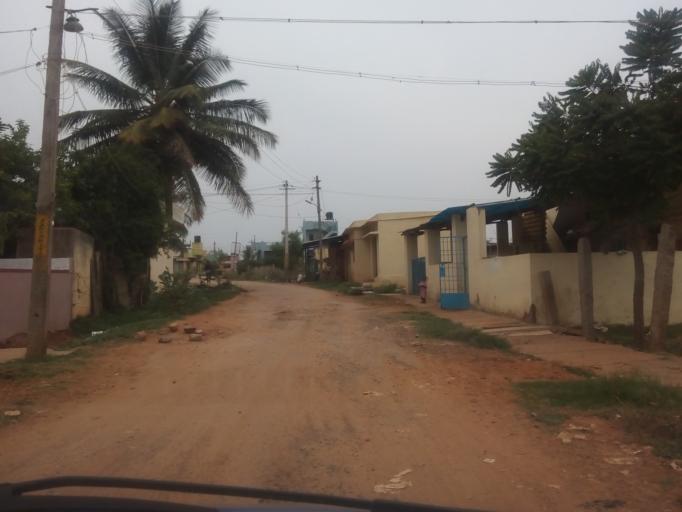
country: IN
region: Karnataka
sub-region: Bangalore Rural
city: Nelamangala
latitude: 12.9936
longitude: 77.4506
